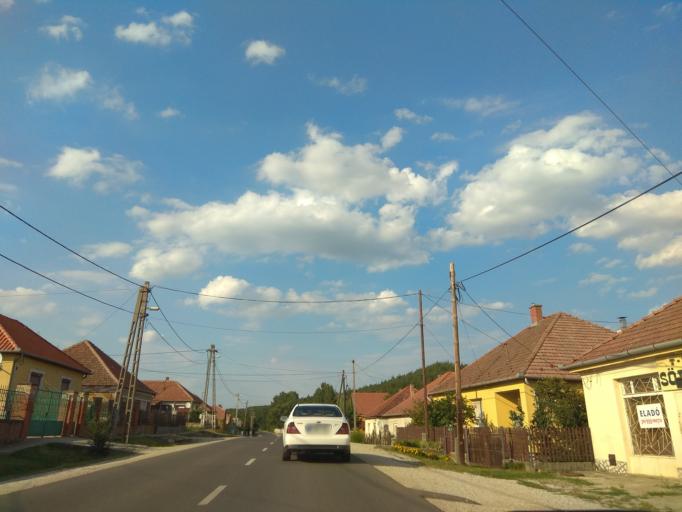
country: HU
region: Borsod-Abauj-Zemplen
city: Harsany
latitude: 47.9750
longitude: 20.7427
